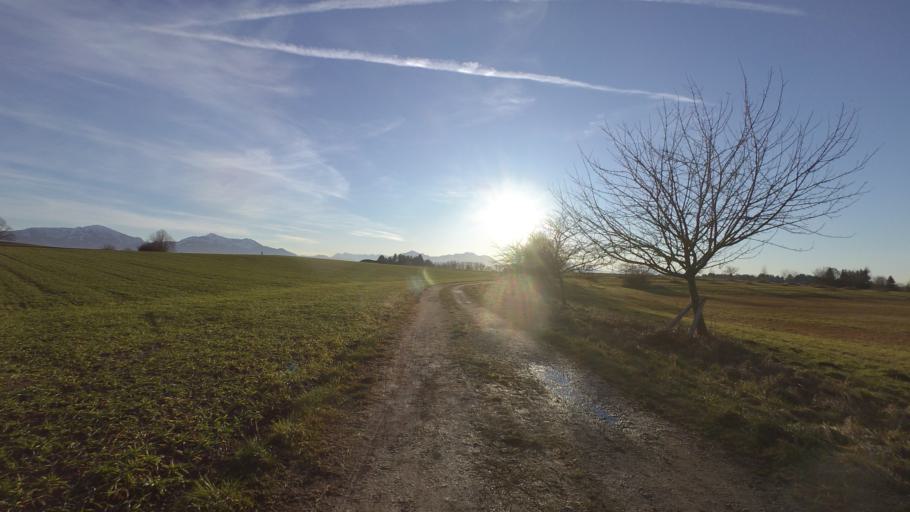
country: DE
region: Bavaria
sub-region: Upper Bavaria
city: Chieming
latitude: 47.9071
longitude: 12.5307
